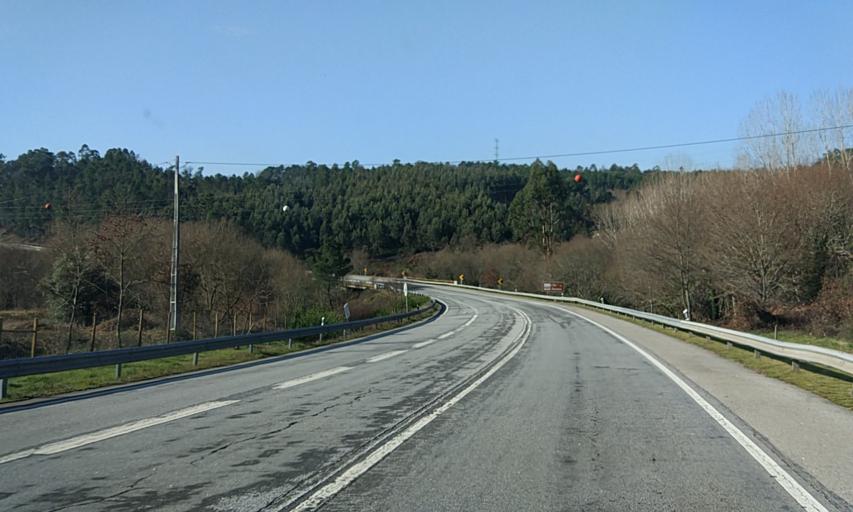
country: PT
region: Viseu
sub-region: Viseu
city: Abraveses
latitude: 40.6685
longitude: -7.9966
